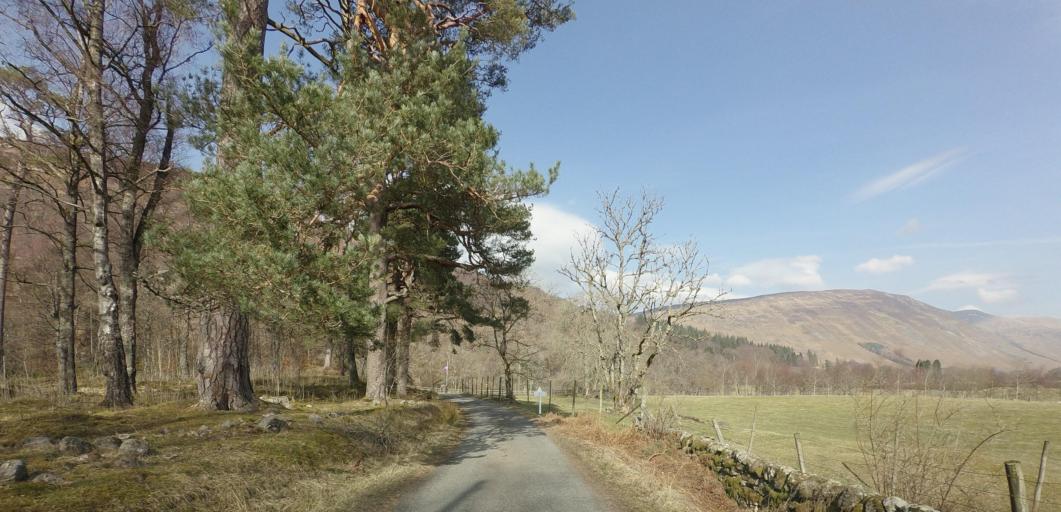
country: GB
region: Scotland
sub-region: Stirling
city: Callander
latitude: 56.5899
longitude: -4.3187
